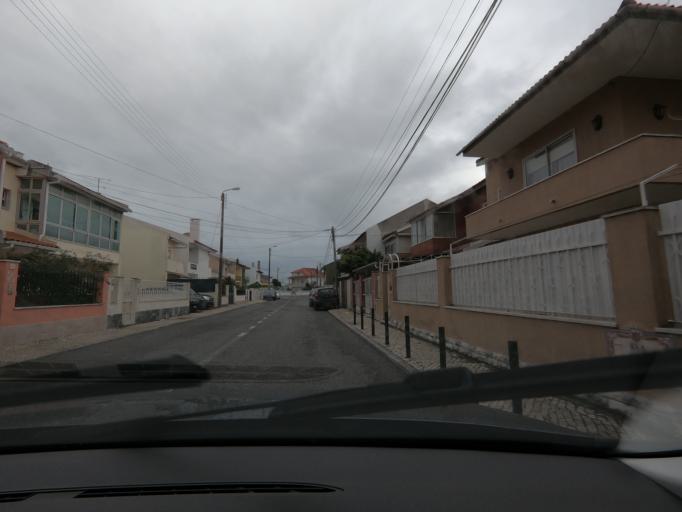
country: PT
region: Lisbon
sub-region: Cascais
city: Sao Domingos de Rana
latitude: 38.7255
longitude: -9.3321
